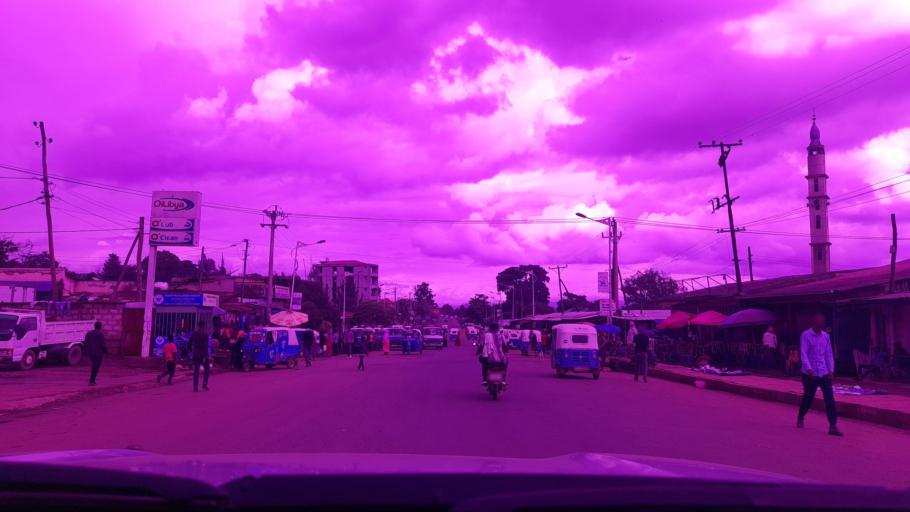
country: ET
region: Oromiya
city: Jima
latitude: 7.6731
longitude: 36.8543
